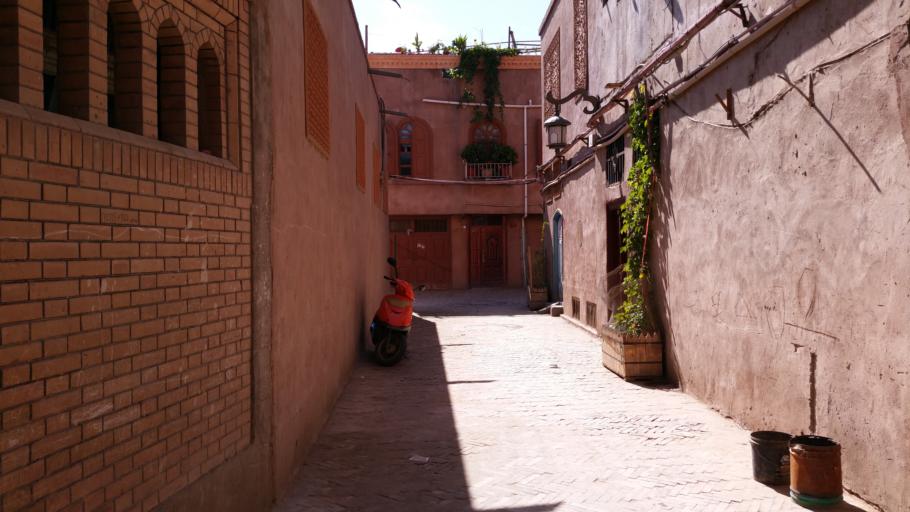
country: CN
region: Xinjiang Uygur Zizhiqu
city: Kashi
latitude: 39.4691
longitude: 75.9821
